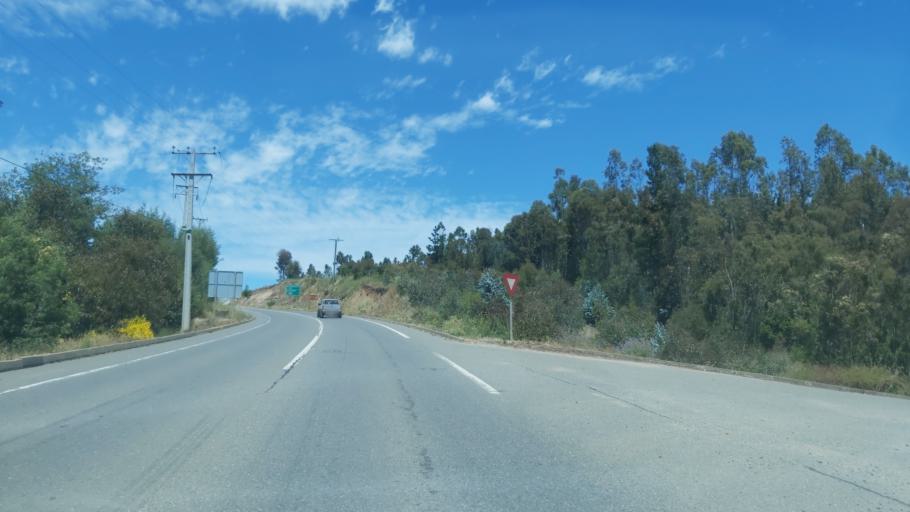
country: CL
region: Maule
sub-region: Provincia de Talca
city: Constitucion
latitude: -35.3156
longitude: -72.3851
